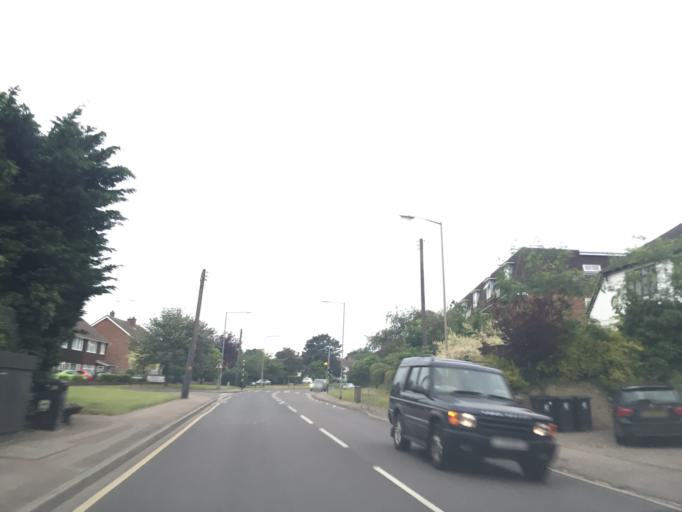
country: GB
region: England
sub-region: Essex
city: Chipping Ongar
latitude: 51.7089
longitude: 0.2446
